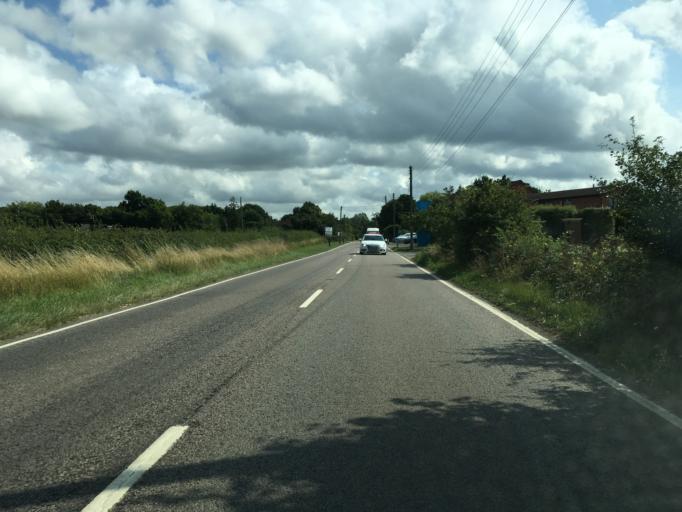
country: GB
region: England
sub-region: Kent
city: Headcorn
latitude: 51.1281
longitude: 0.6464
